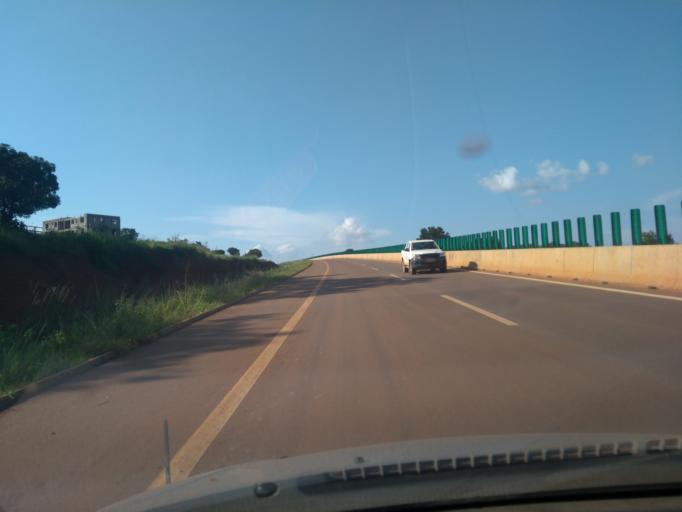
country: UG
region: Central Region
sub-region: Wakiso District
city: Kajansi
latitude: 0.1856
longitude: 32.5237
